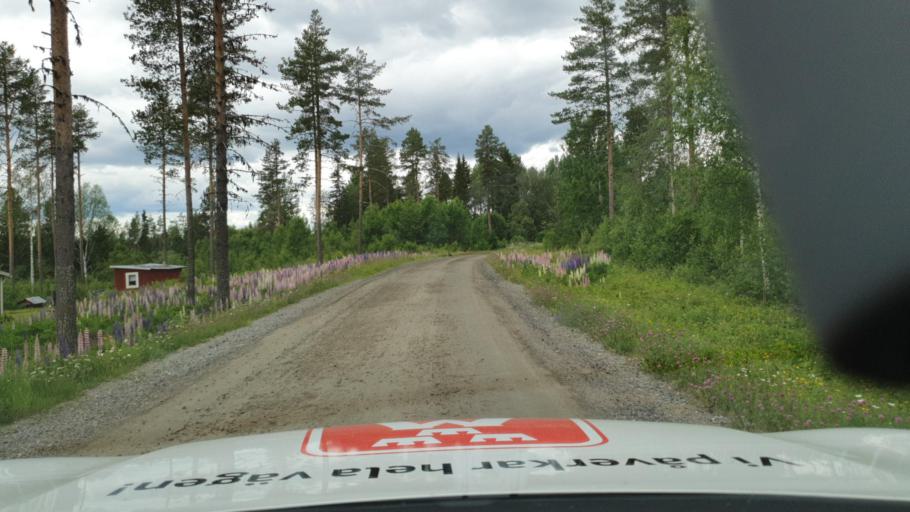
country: SE
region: Vaesterbotten
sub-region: Bjurholms Kommun
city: Bjurholm
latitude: 63.7963
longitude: 19.0880
